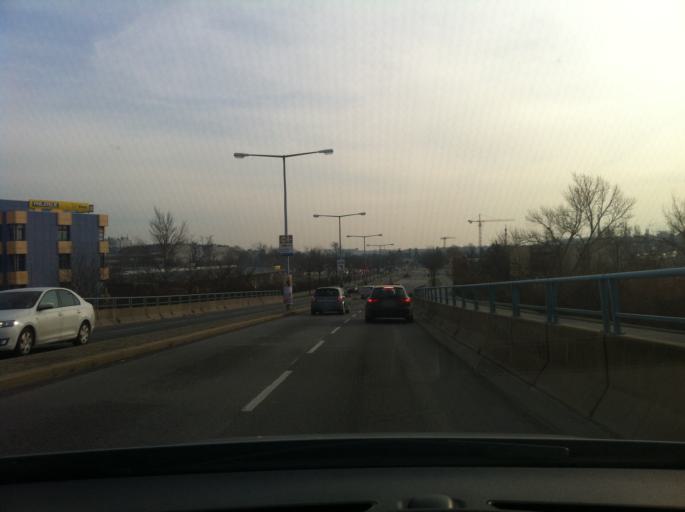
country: AT
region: Vienna
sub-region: Wien Stadt
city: Vienna
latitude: 48.2619
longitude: 16.4095
